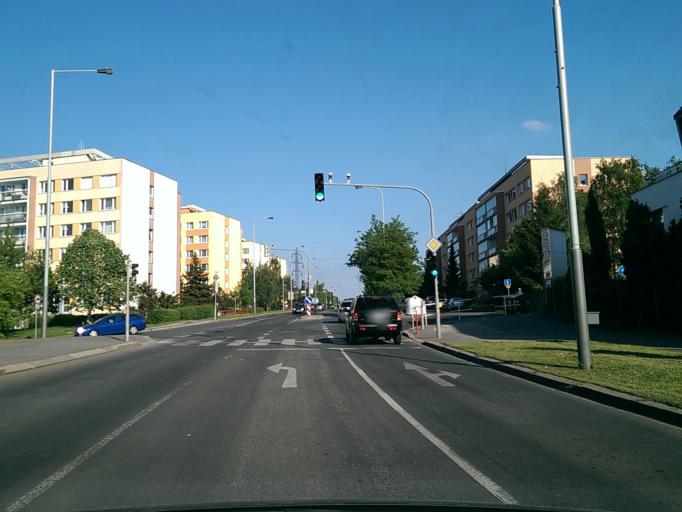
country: CZ
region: Praha
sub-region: Praha 14
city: Hostavice
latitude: 50.0489
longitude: 14.5426
